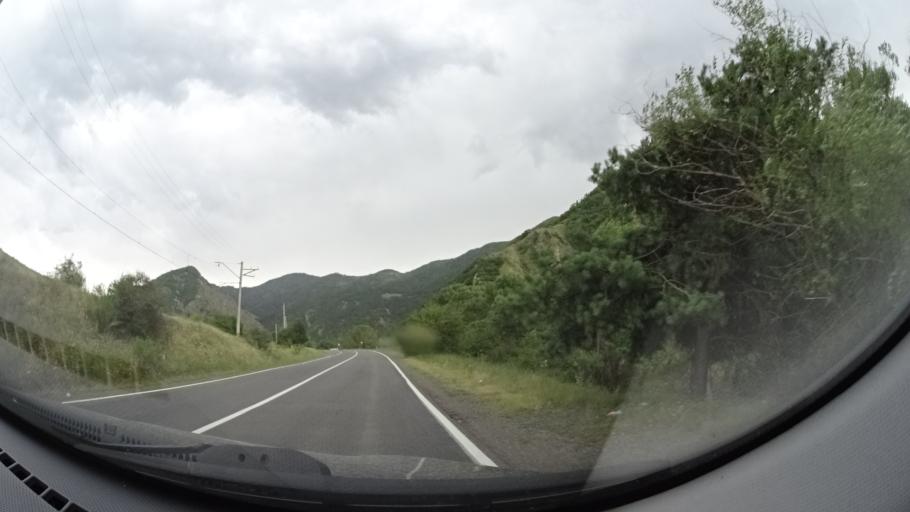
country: GE
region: Samtskhe-Javakheti
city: Aspindza
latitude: 41.7443
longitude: 43.1959
